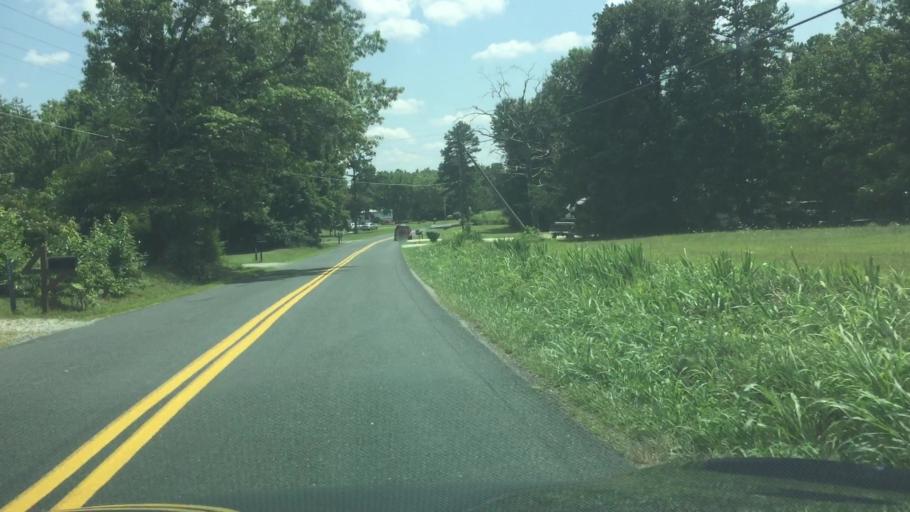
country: US
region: Virginia
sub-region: Appomattox County
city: Appomattox
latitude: 37.3001
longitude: -78.8487
